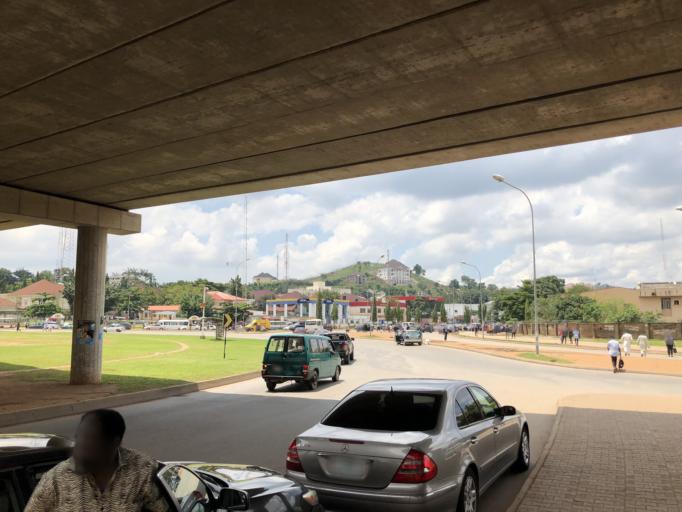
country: NG
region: Abuja Federal Capital Territory
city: Abuja
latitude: 9.0500
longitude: 7.5257
